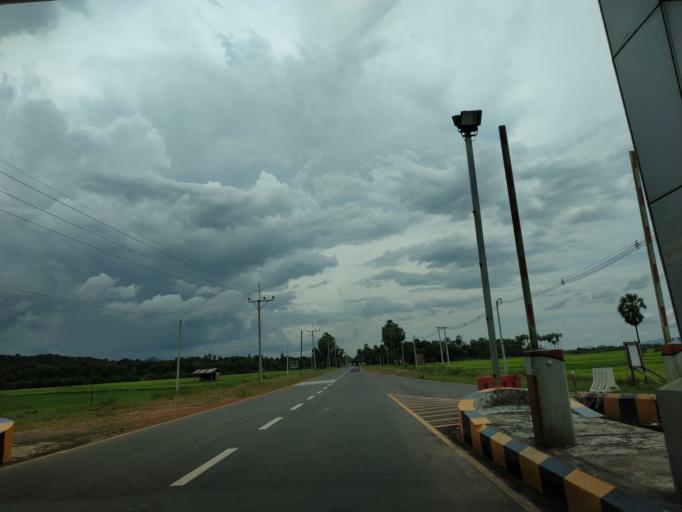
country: MM
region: Tanintharyi
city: Dawei
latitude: 14.0234
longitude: 98.2247
